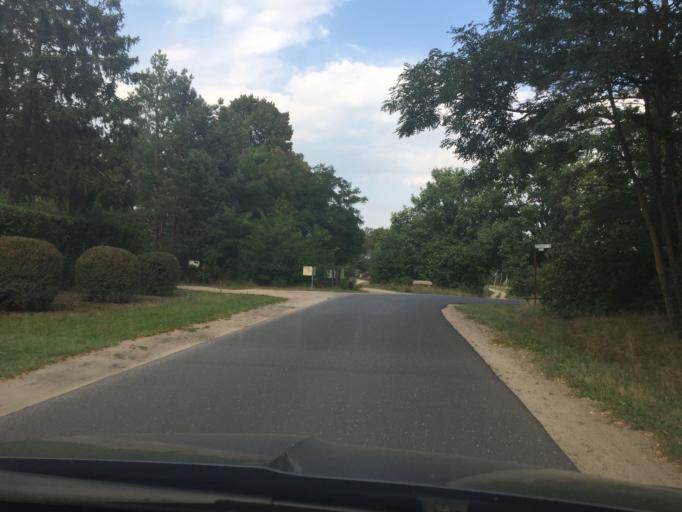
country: DE
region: Brandenburg
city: Grunheide
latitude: 52.3735
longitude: 13.7882
